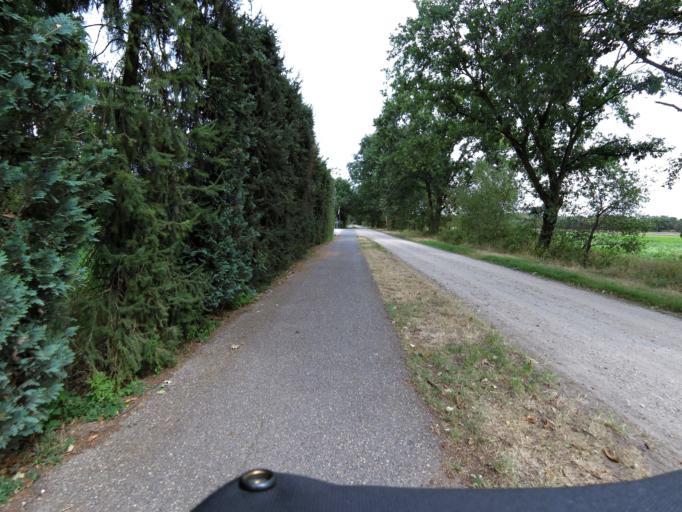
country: NL
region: Limburg
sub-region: Gemeente Bergen
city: Wellerlooi
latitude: 51.5801
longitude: 6.1148
